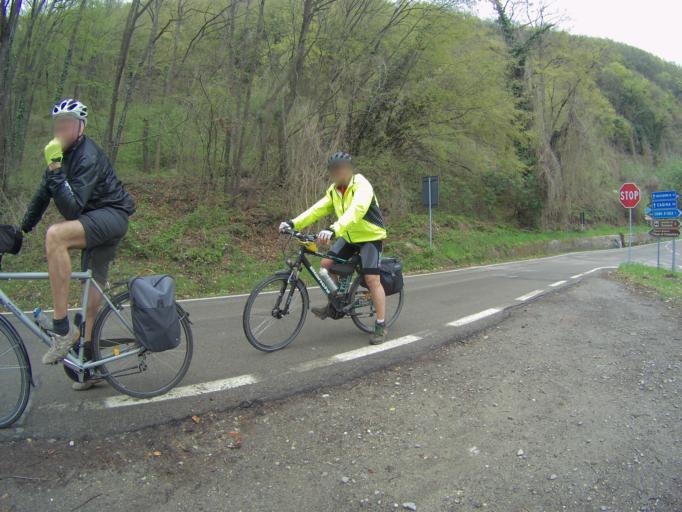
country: IT
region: Emilia-Romagna
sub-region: Provincia di Reggio Emilia
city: Ciano d'Enza
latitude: 44.5686
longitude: 10.4498
